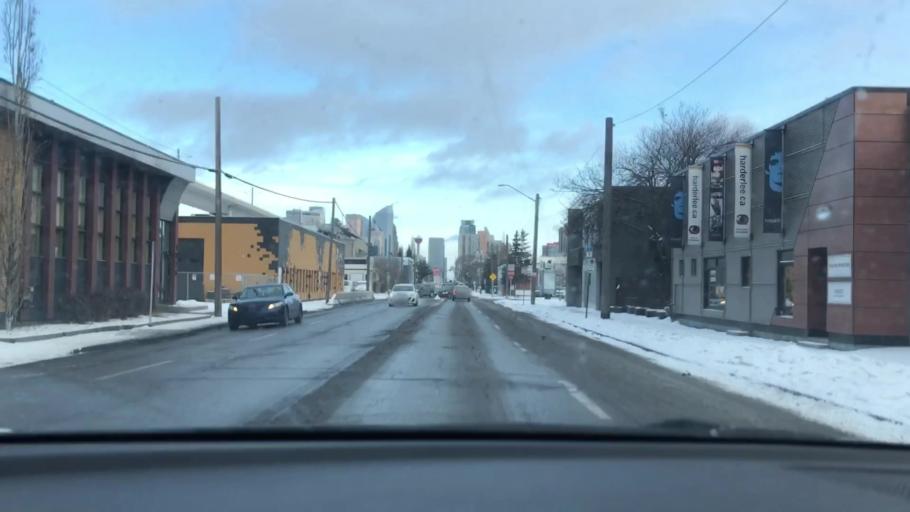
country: CA
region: Alberta
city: Calgary
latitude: 51.0445
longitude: -114.1055
